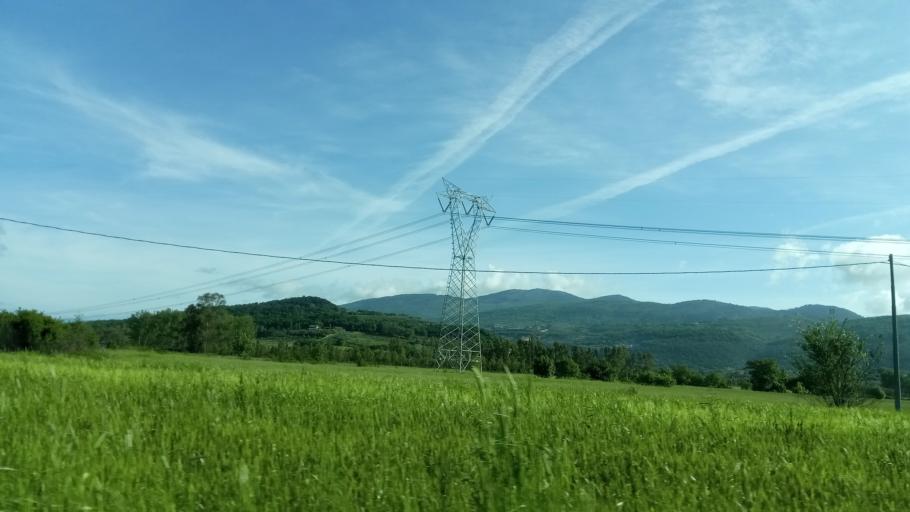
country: IT
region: Latium
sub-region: Provincia di Latina
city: Grunuovo-Campomaggiore San Luca
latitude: 41.2842
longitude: 13.7695
